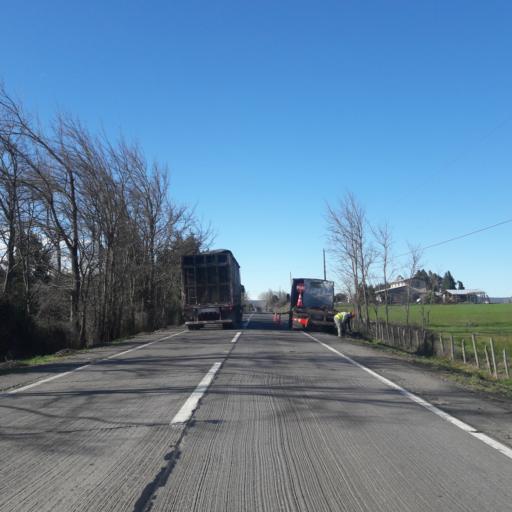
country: CL
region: Araucania
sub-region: Provincia de Malleco
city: Angol
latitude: -37.7793
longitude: -72.5366
